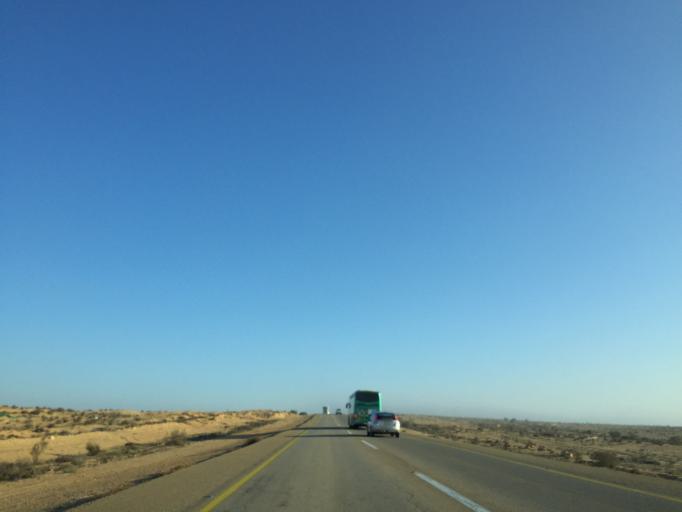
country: IL
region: Southern District
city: Yeroham
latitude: 31.0208
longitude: 34.9647
